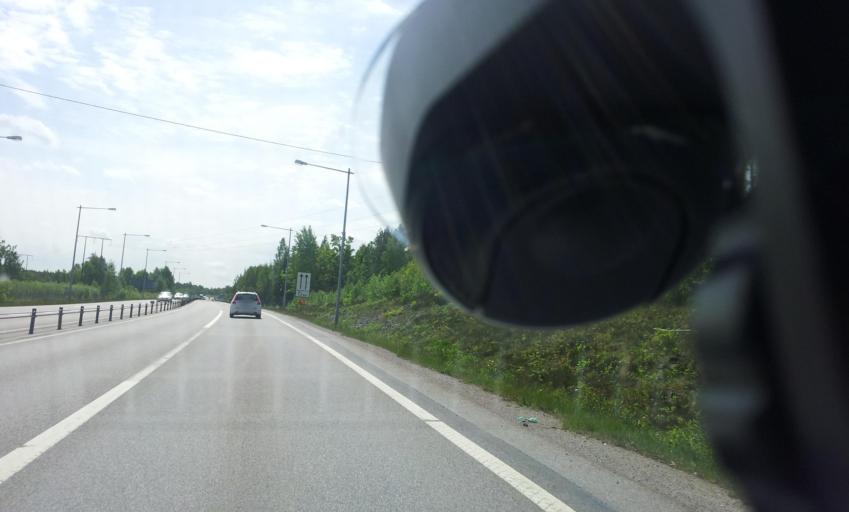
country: SE
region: Kalmar
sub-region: Vasterviks Kommun
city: Vaestervik
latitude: 57.7603
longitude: 16.5562
